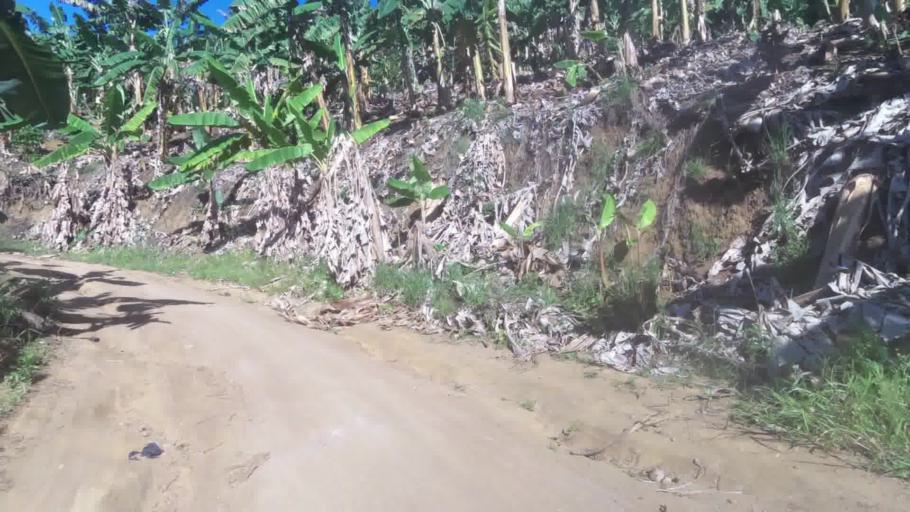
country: BR
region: Espirito Santo
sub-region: Iconha
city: Iconha
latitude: -20.7551
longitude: -40.8105
